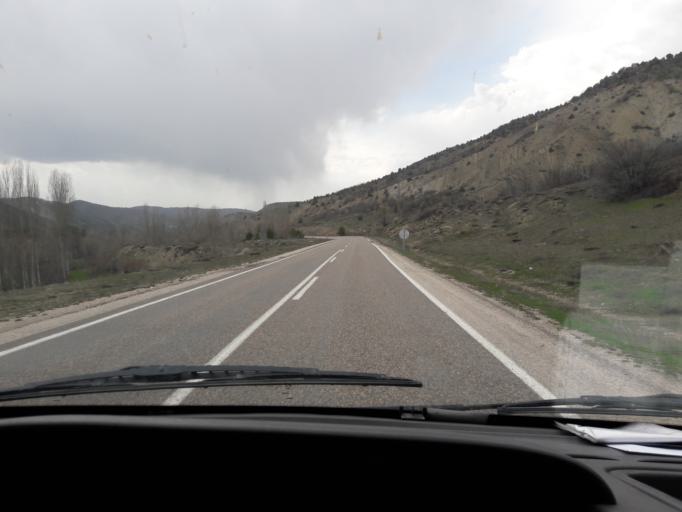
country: TR
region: Giresun
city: Alucra
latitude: 40.2734
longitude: 38.8586
